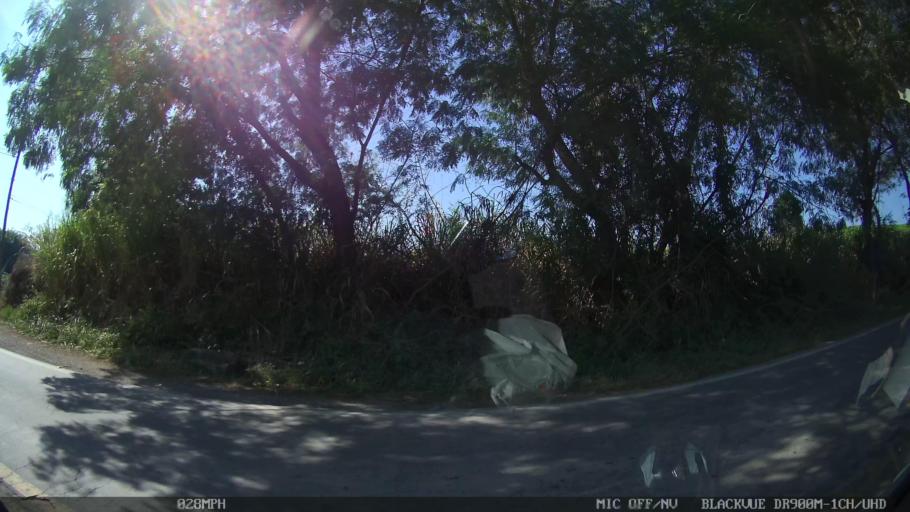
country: BR
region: Sao Paulo
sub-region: Campinas
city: Campinas
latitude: -22.9932
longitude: -47.0858
